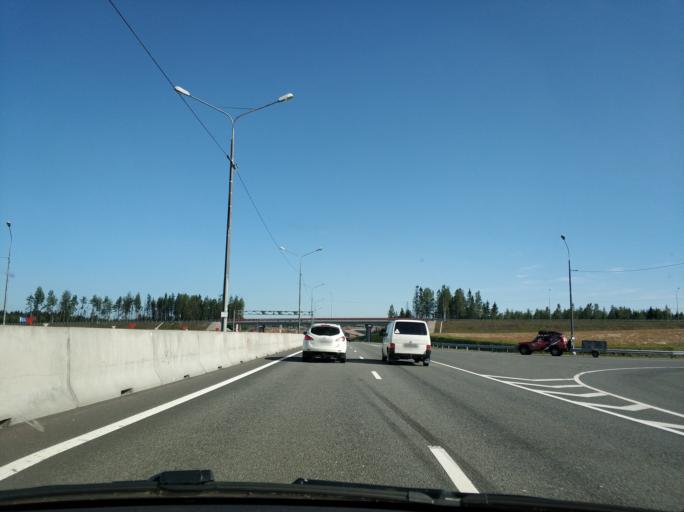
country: RU
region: Leningrad
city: Sosnovo
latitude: 60.5006
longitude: 30.1955
